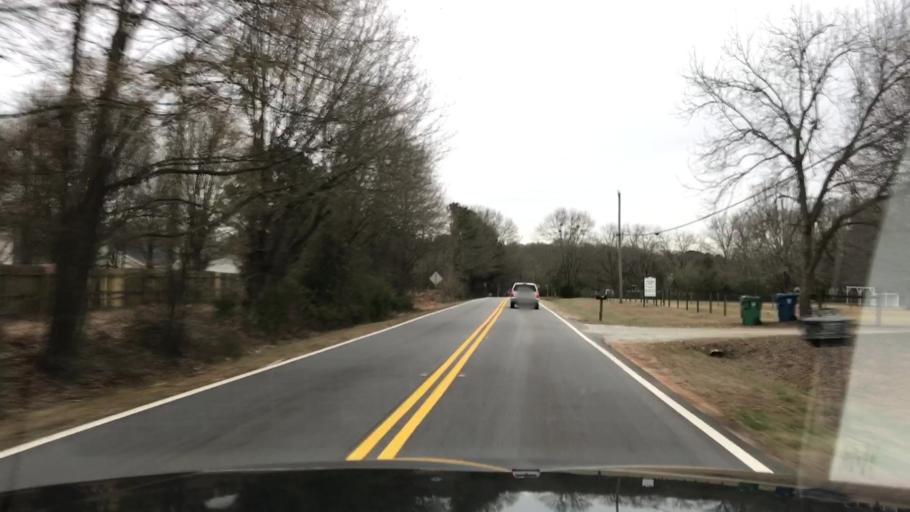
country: US
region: Georgia
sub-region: Walton County
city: Monroe
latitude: 33.8444
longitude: -83.7362
